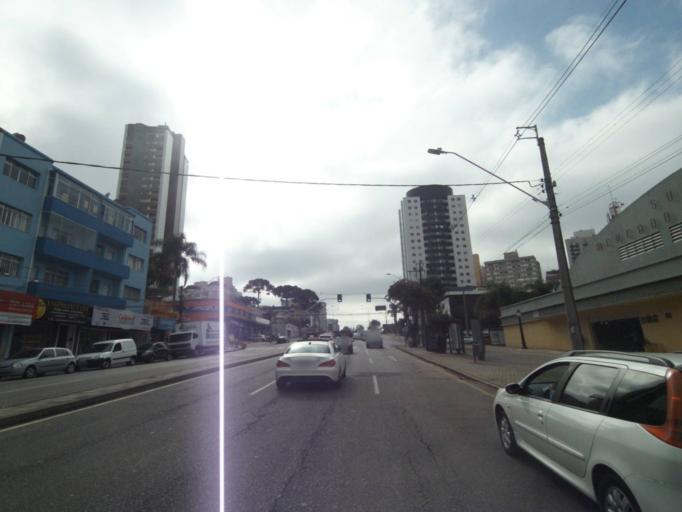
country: BR
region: Parana
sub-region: Curitiba
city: Curitiba
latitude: -25.4340
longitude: -49.2572
